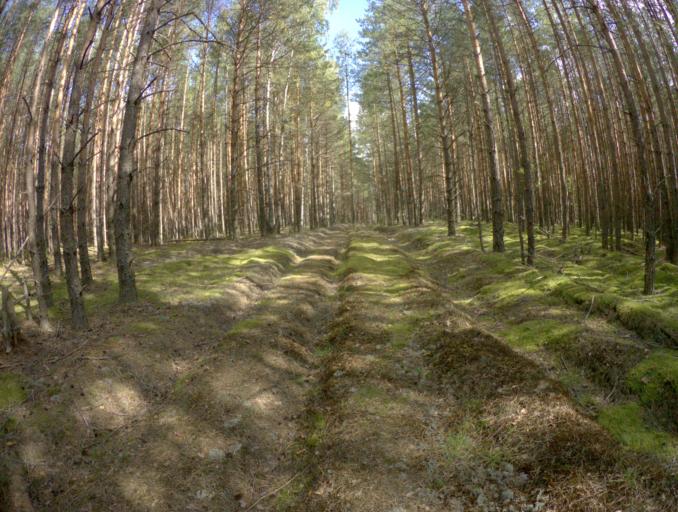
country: RU
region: Vladimir
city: Pokrov
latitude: 55.8457
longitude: 39.2422
